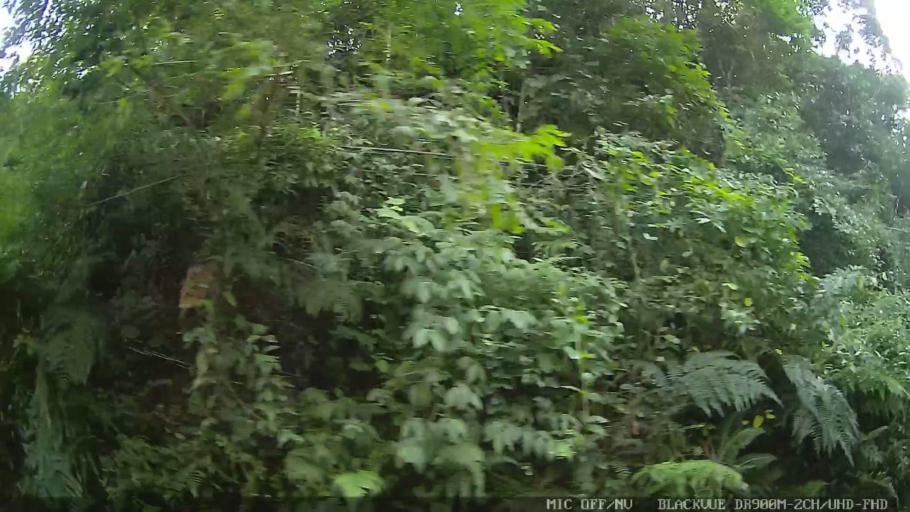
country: BR
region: Sao Paulo
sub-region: Guaruja
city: Guaruja
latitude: -24.0107
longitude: -46.2797
